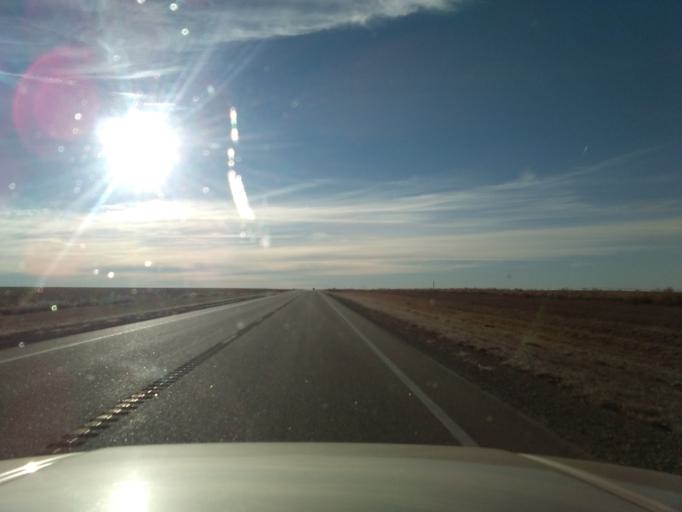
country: US
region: Kansas
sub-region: Sheridan County
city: Hoxie
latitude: 39.5265
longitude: -100.6088
